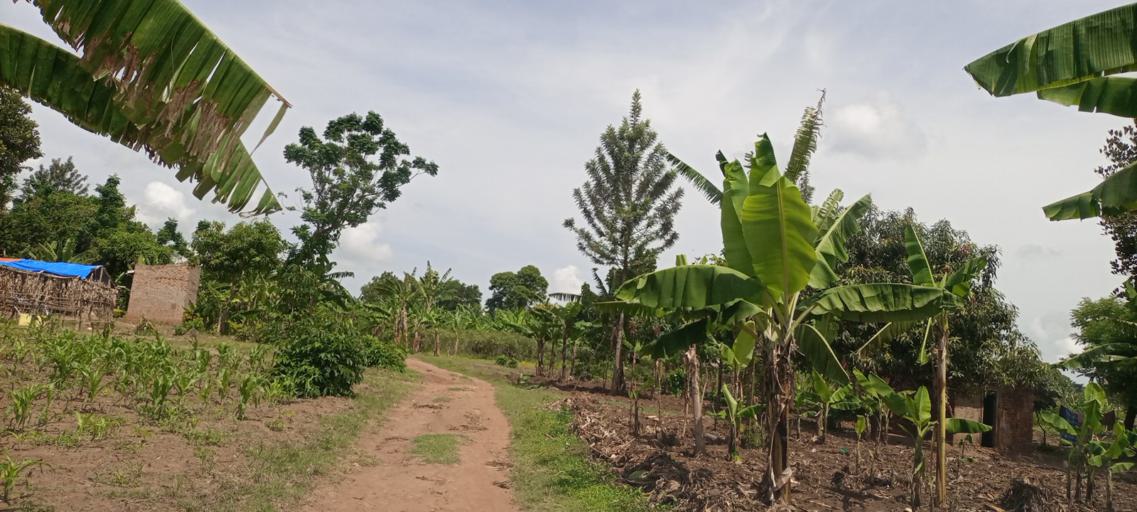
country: UG
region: Eastern Region
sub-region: Budaka District
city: Budaka
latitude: 1.1713
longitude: 33.9470
